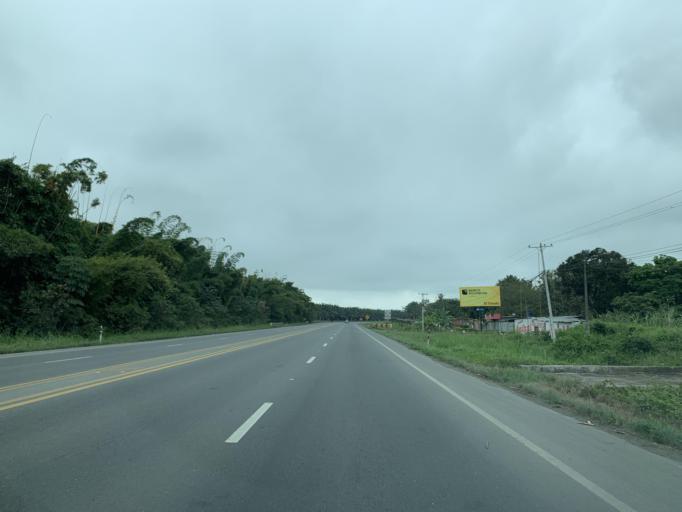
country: EC
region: Guayas
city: Coronel Marcelino Mariduena
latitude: -2.3250
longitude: -79.4505
